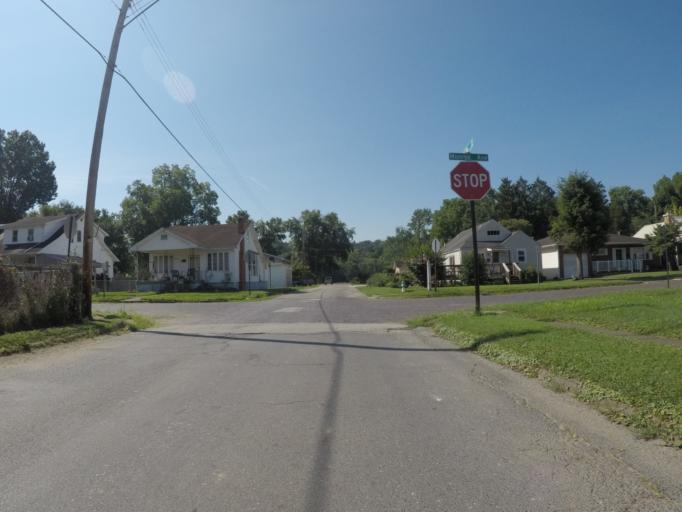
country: US
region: West Virginia
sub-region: Cabell County
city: Huntington
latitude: 38.4064
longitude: -82.4860
